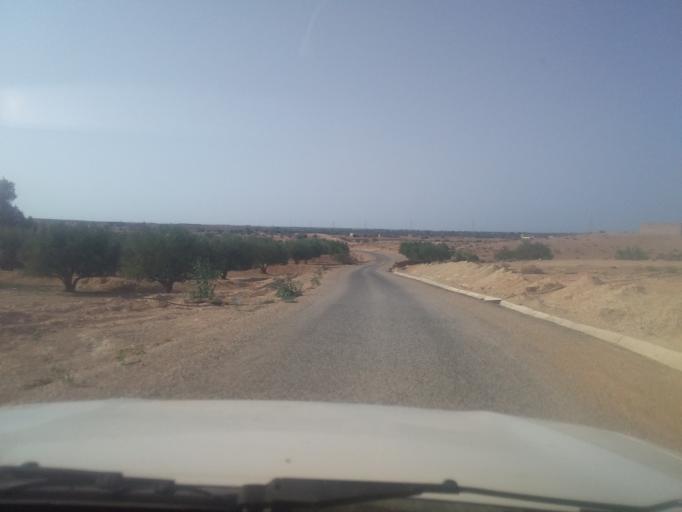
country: TN
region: Qabis
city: Matmata
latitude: 33.5833
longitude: 10.2600
